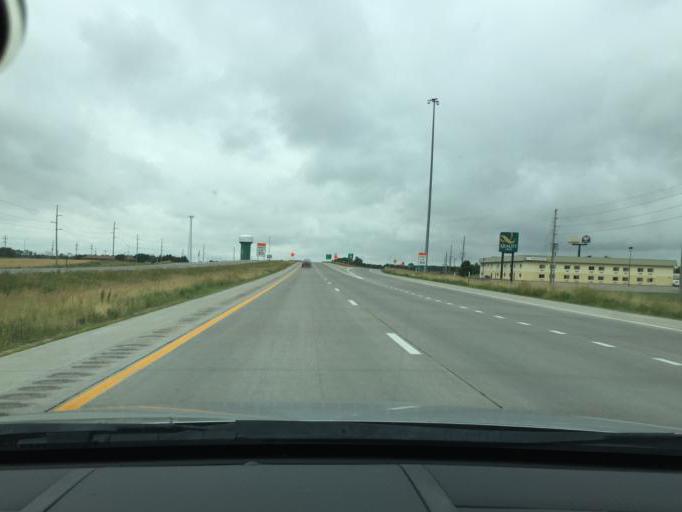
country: US
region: Kansas
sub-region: Reno County
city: South Hutchinson
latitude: 38.0133
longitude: -97.9357
